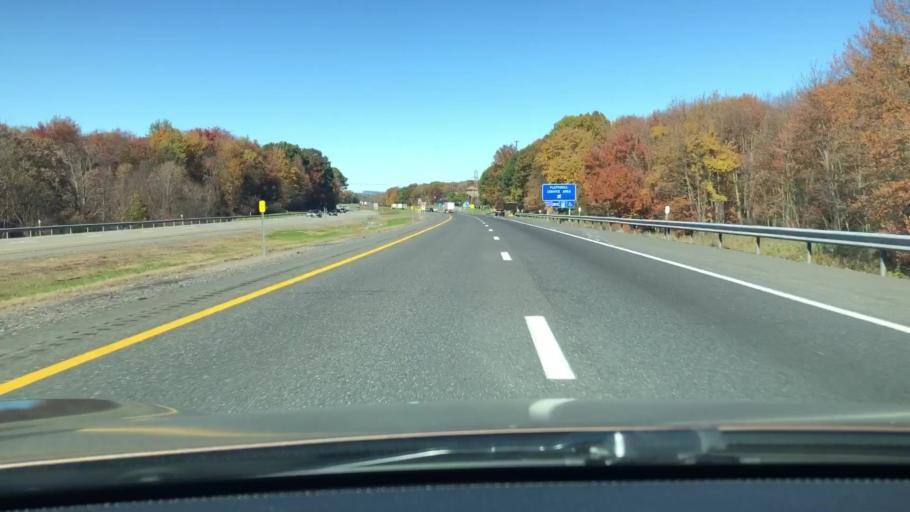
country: US
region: New York
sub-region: Orange County
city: Orange Lake
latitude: 41.5723
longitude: -74.0844
